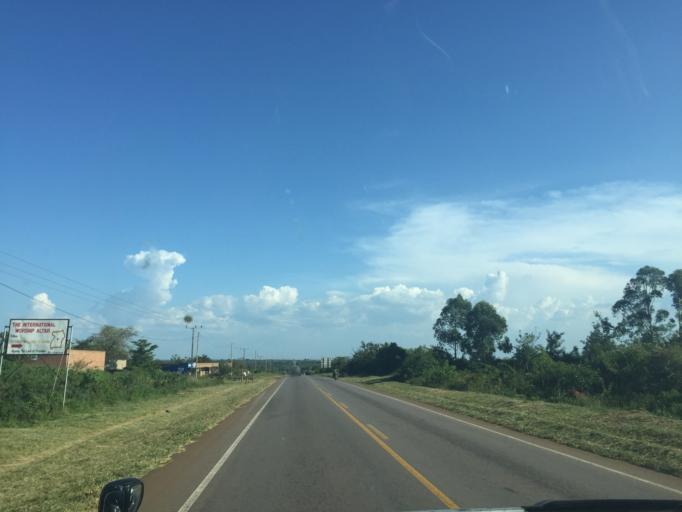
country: UG
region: Central Region
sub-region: Nakasongola District
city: Nakasongola
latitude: 1.2794
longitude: 32.4366
